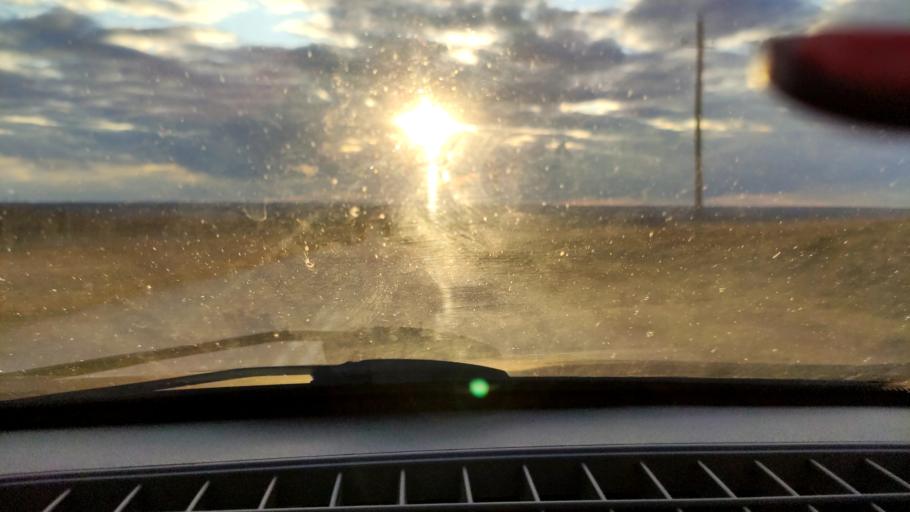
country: RU
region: Bashkortostan
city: Tolbazy
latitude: 54.0106
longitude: 55.5834
